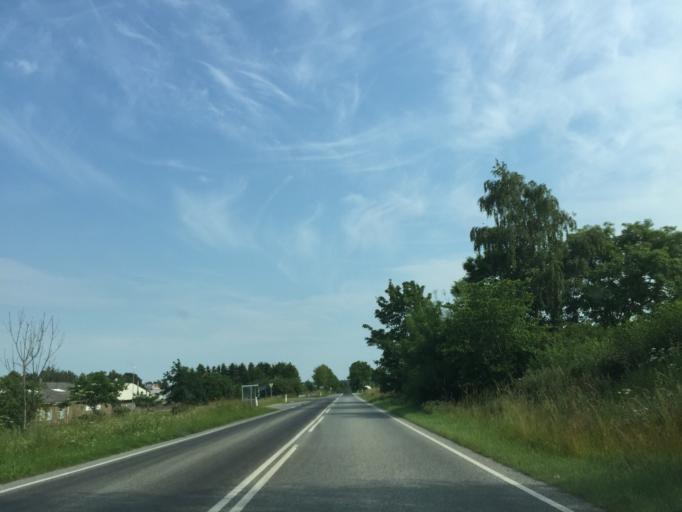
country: DK
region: Central Jutland
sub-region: Syddjurs Kommune
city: Ronde
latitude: 56.3094
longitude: 10.4434
